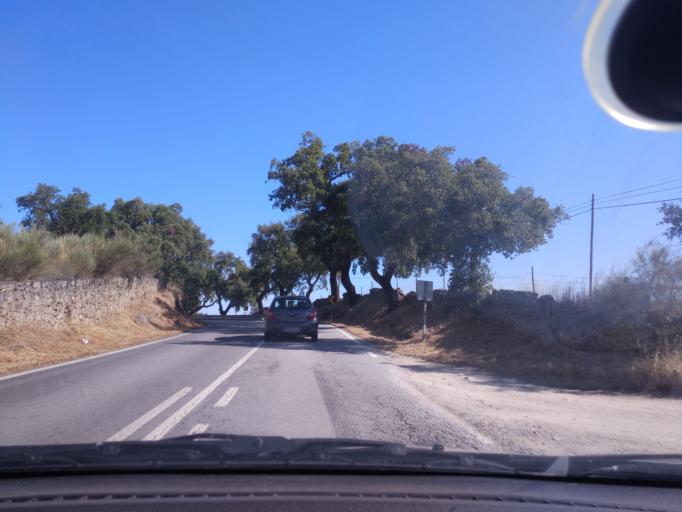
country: PT
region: Portalegre
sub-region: Nisa
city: Nisa
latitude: 39.4871
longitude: -7.6362
